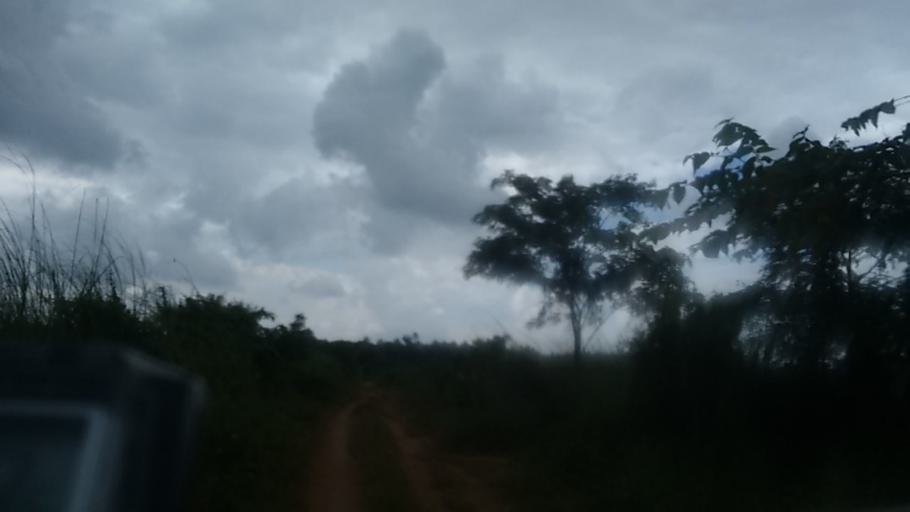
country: IN
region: Kerala
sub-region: Thrissur District
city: Trichur
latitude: 10.5301
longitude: 76.1659
